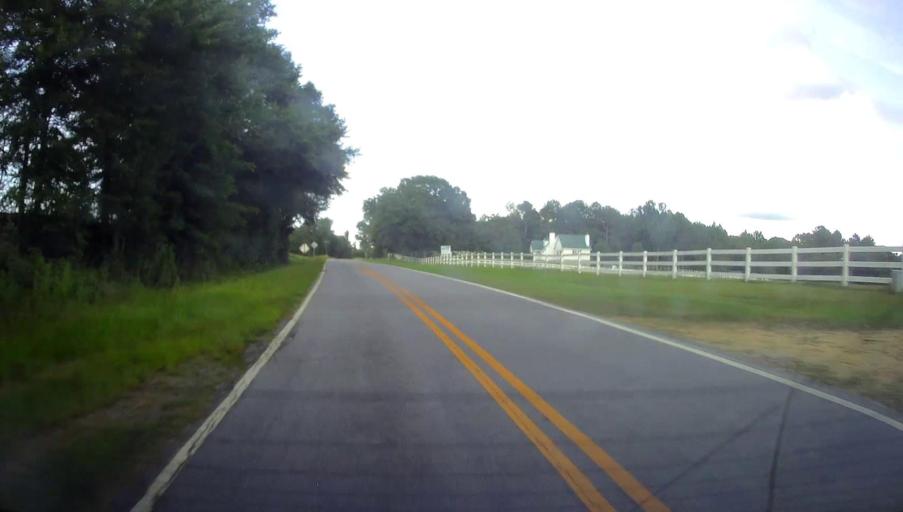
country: US
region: Georgia
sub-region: Crawford County
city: Knoxville
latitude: 32.7528
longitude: -83.9120
